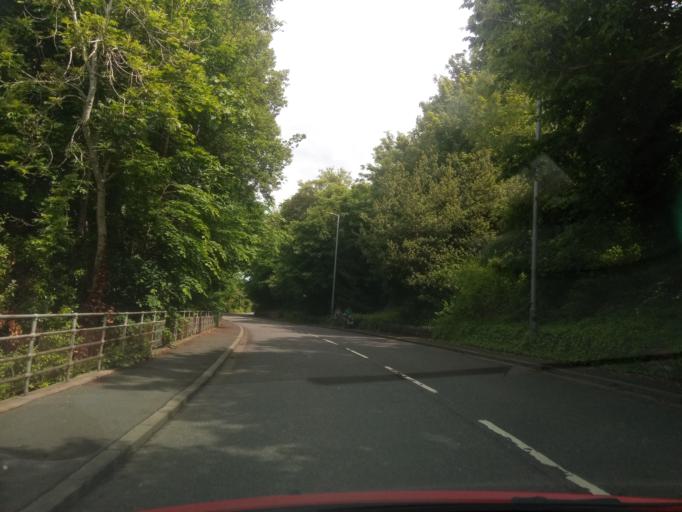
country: GB
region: Scotland
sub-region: The Scottish Borders
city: Selkirk
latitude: 55.5533
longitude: -2.8385
